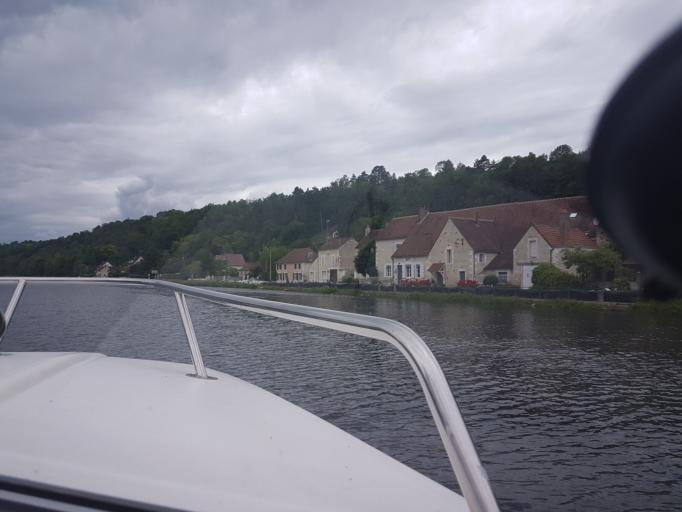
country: FR
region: Bourgogne
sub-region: Departement de l'Yonne
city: Champs-sur-Yonne
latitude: 47.7541
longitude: 3.5908
